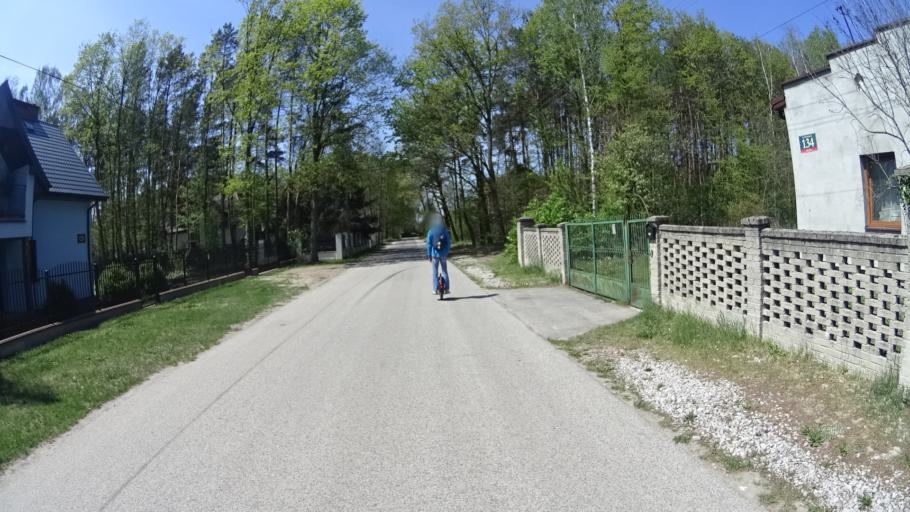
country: PL
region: Masovian Voivodeship
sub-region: Powiat warszawski zachodni
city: Truskaw
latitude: 52.2847
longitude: 20.7258
